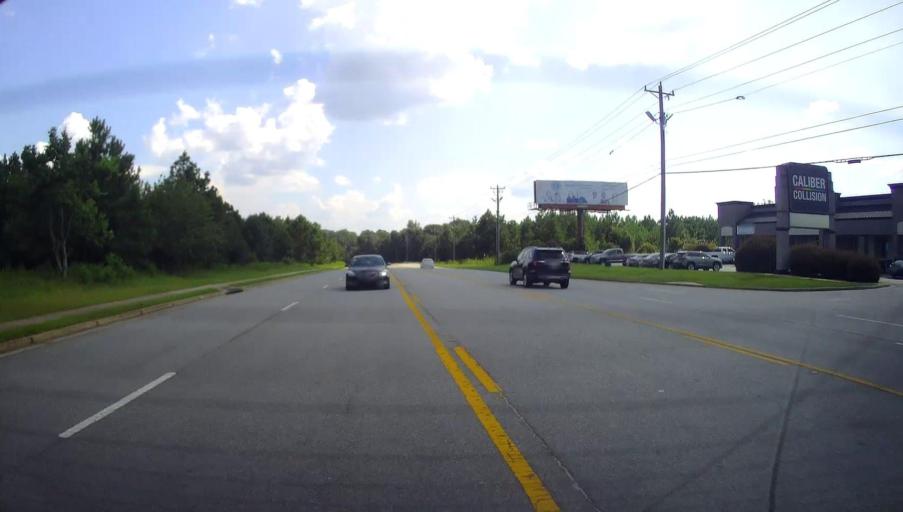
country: US
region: Georgia
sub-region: Houston County
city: Centerville
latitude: 32.6150
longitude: -83.6693
